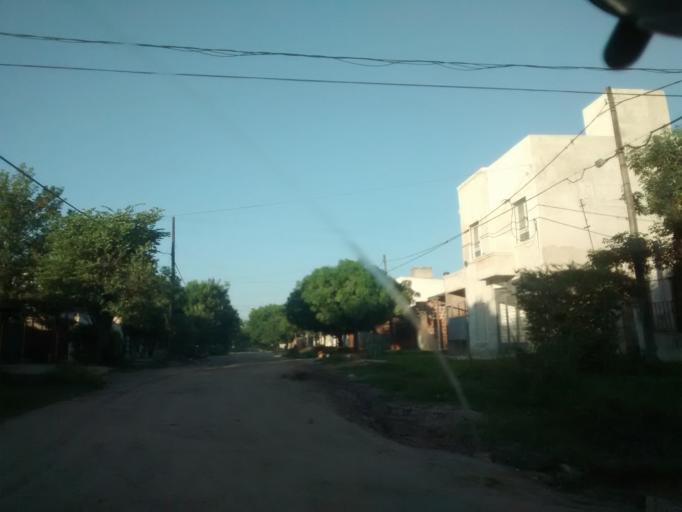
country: AR
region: Chaco
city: Resistencia
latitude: -27.4633
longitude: -58.9693
